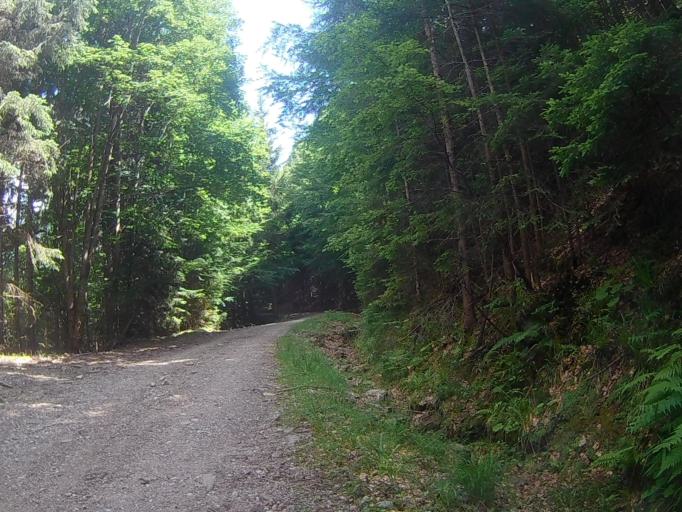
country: SI
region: Selnica ob Dravi
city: Selnica ob Dravi
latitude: 46.5090
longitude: 15.4793
